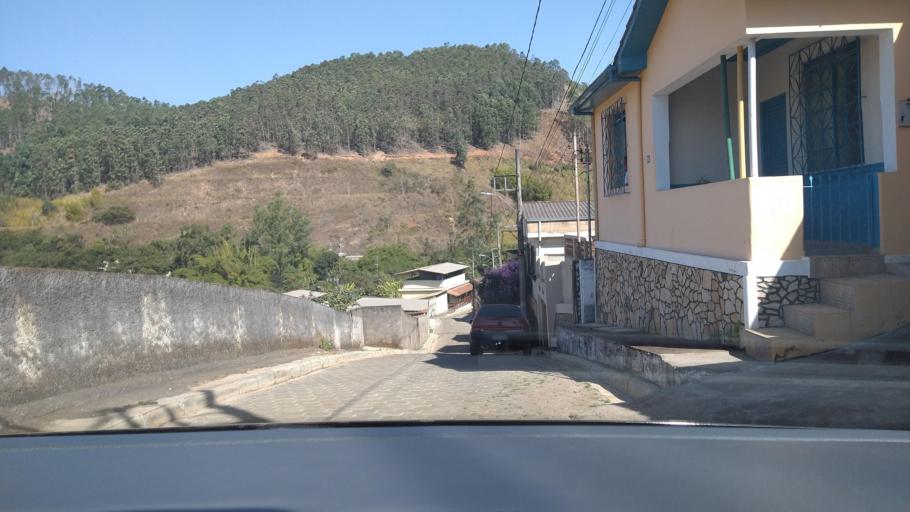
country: BR
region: Minas Gerais
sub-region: Rio Piracicaba
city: Rio Piracicaba
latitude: -19.9359
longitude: -43.1764
